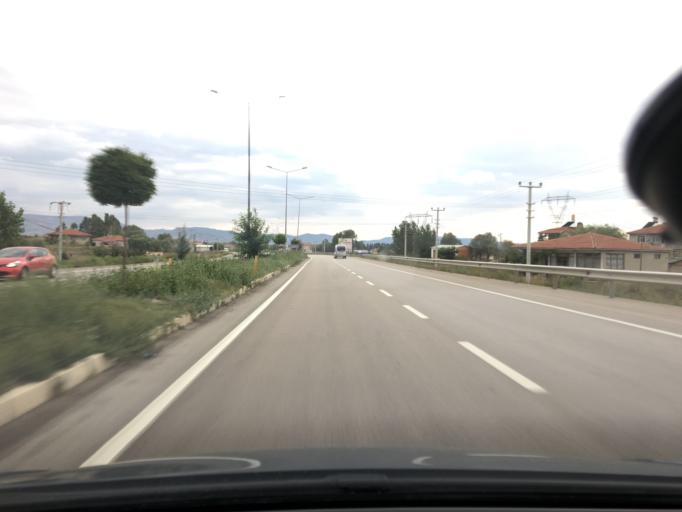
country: TR
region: Afyonkarahisar
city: Sincanli
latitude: 38.7880
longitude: 30.3792
